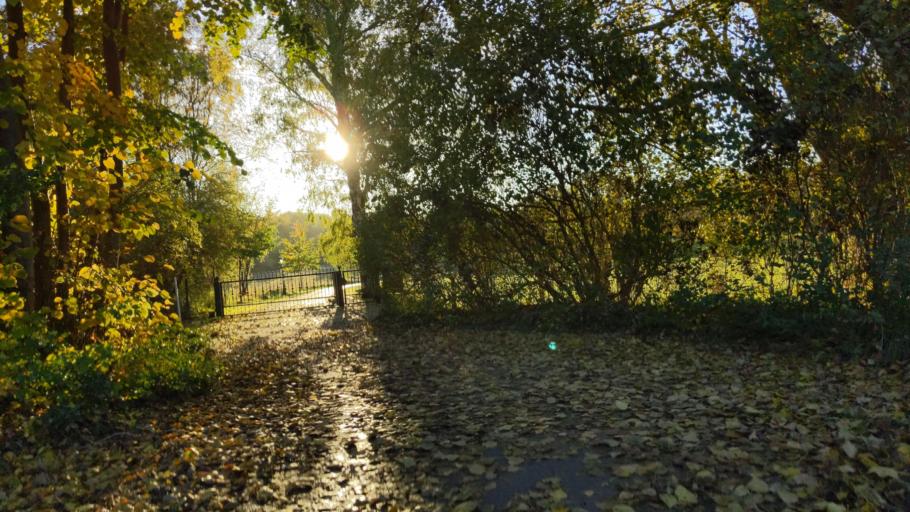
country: DE
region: Schleswig-Holstein
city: Gross Gronau
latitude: 53.8448
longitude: 10.7307
